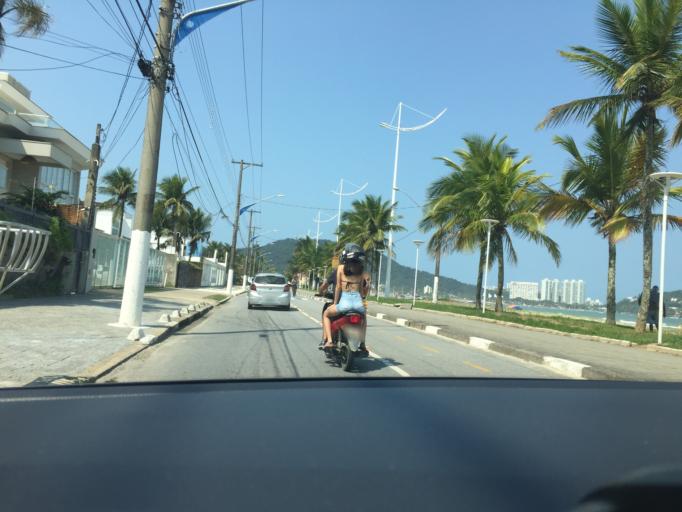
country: BR
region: Sao Paulo
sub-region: Guaruja
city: Guaruja
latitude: -23.9848
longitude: -46.2186
